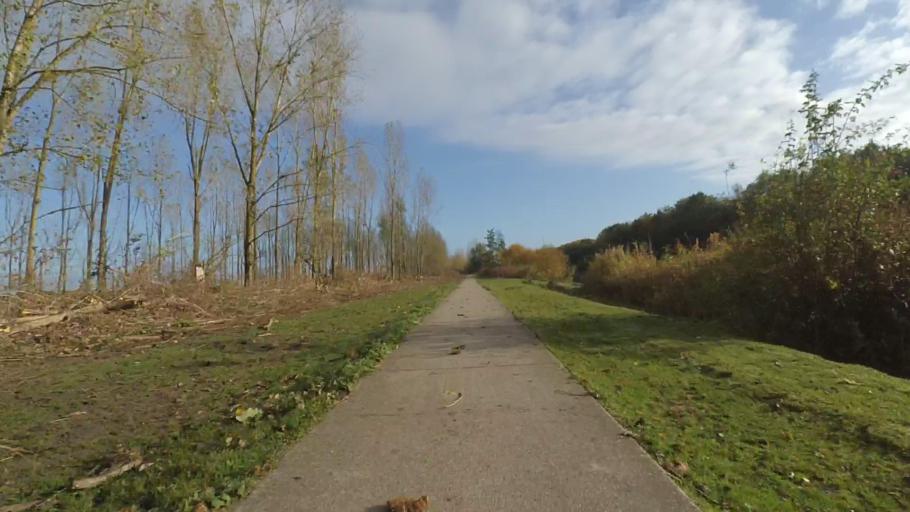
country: NL
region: Utrecht
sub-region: Gemeente Bunschoten
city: Spakenburg
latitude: 52.3199
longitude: 5.3998
